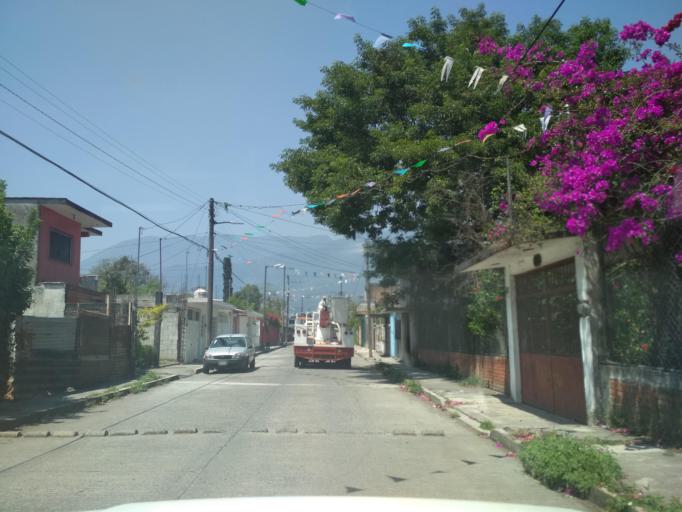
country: MX
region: Veracruz
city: Rio Blanco
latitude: 18.8333
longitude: -97.1122
